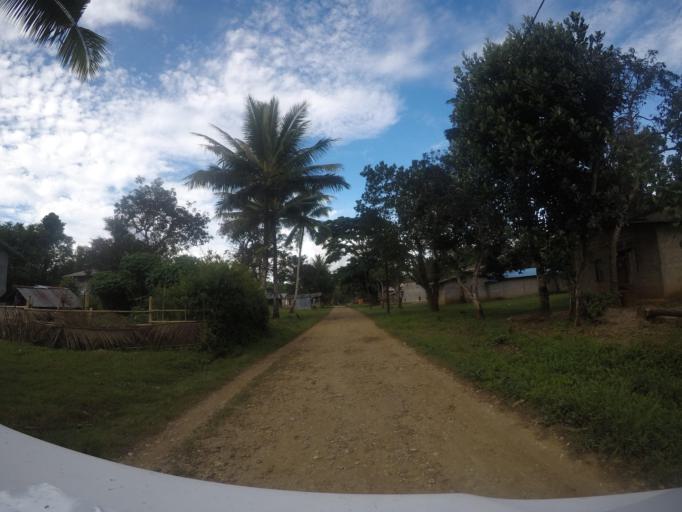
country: TL
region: Lautem
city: Lospalos
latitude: -8.5019
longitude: 126.9941
